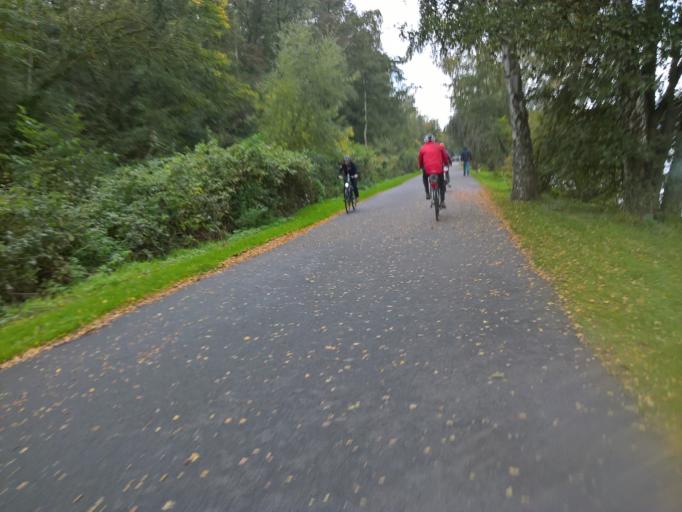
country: DE
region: North Rhine-Westphalia
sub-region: Regierungsbezirk Dusseldorf
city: Velbert
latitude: 51.3953
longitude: 7.0533
